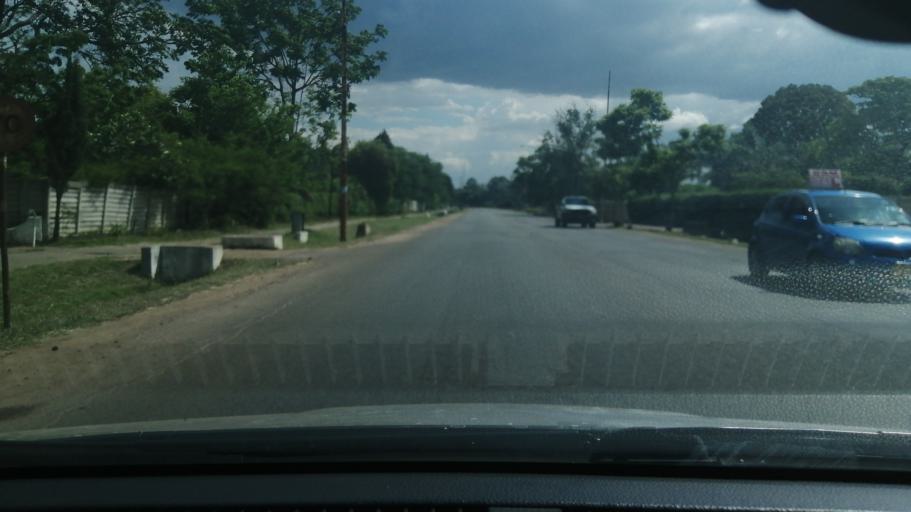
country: ZW
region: Harare
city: Harare
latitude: -17.8149
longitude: 31.0932
